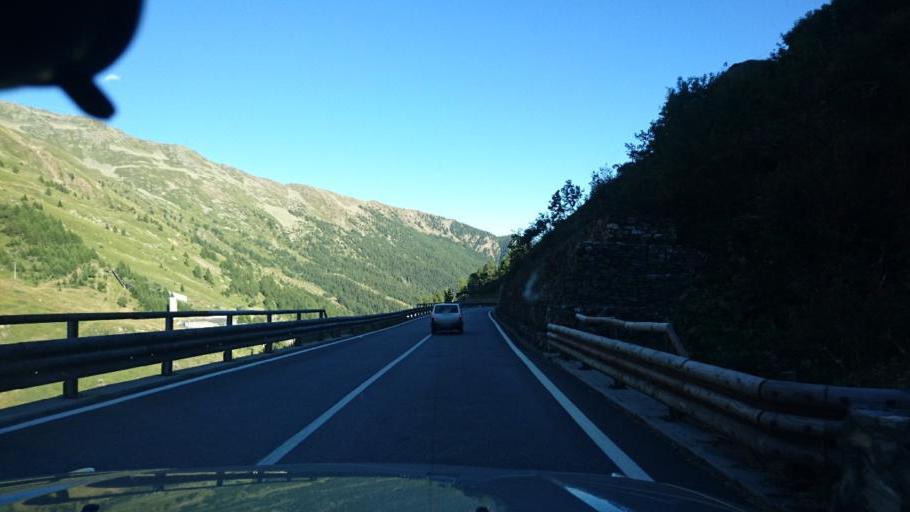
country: IT
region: Aosta Valley
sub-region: Valle d'Aosta
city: San Leonardo
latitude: 45.8520
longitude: 7.1543
